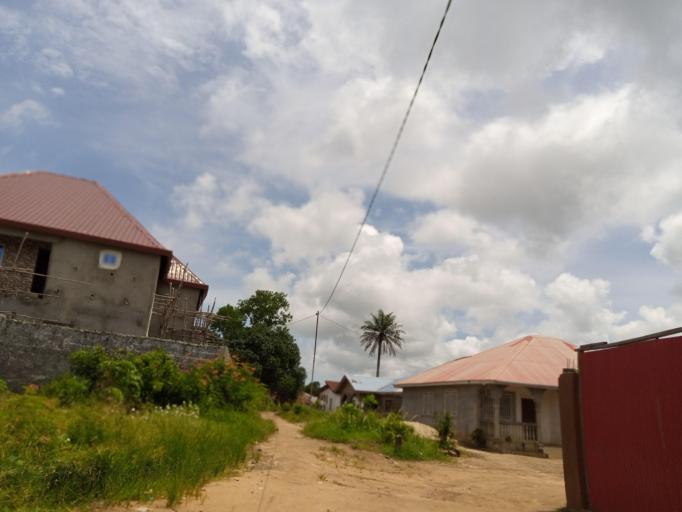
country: SL
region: Northern Province
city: Masoyila
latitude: 8.5955
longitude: -13.1813
